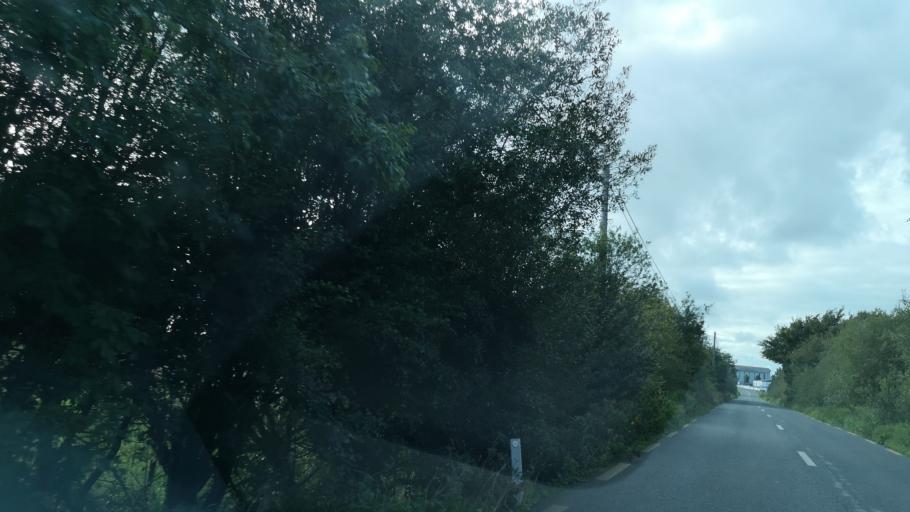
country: IE
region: Connaught
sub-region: County Galway
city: Ballinasloe
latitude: 53.2931
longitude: -8.0970
